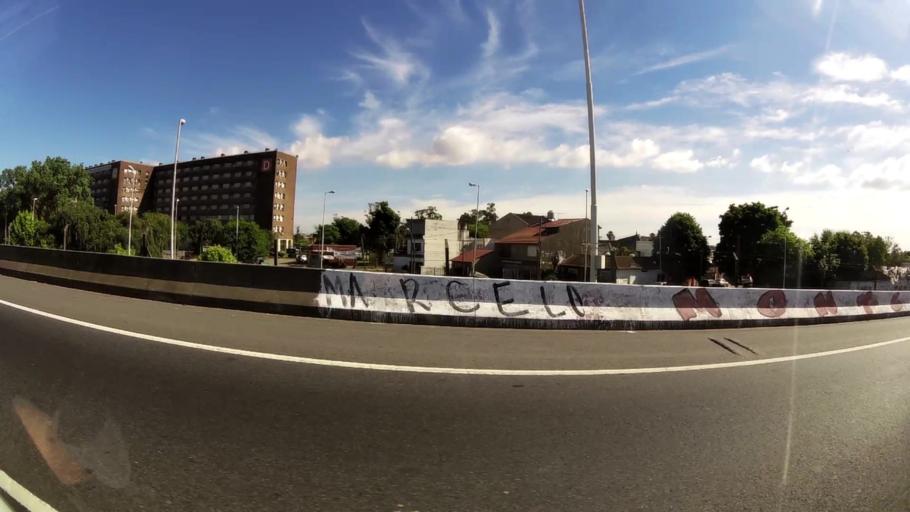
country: AR
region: Buenos Aires
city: Caseros
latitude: -34.6311
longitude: -58.5729
